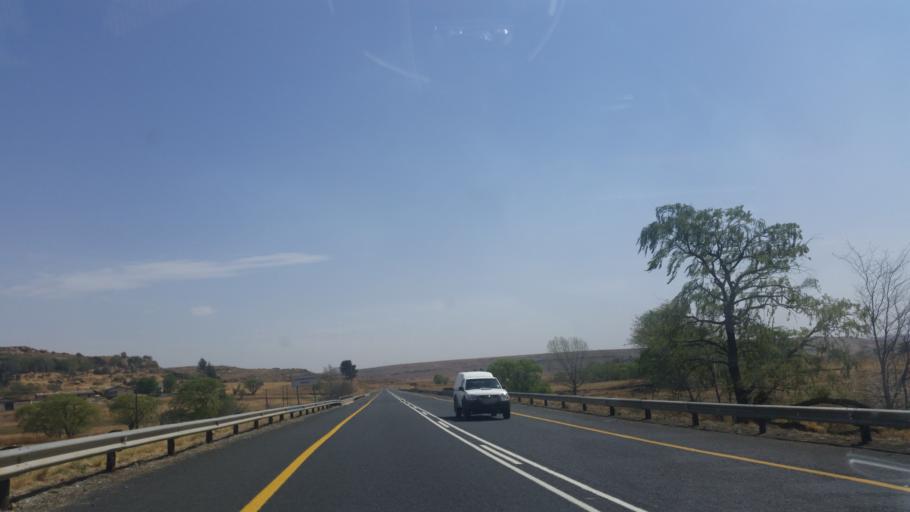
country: ZA
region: Orange Free State
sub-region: Thabo Mofutsanyana District Municipality
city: Bethlehem
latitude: -28.3072
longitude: 28.5007
